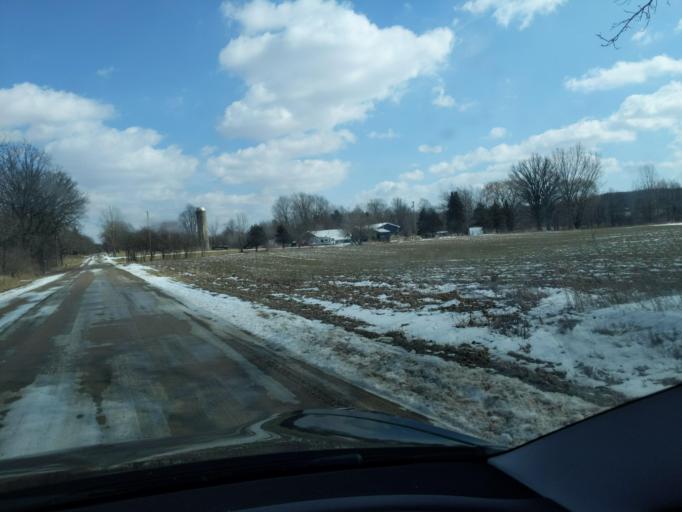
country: US
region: Michigan
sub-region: Ingham County
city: Webberville
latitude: 42.6139
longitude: -84.1366
